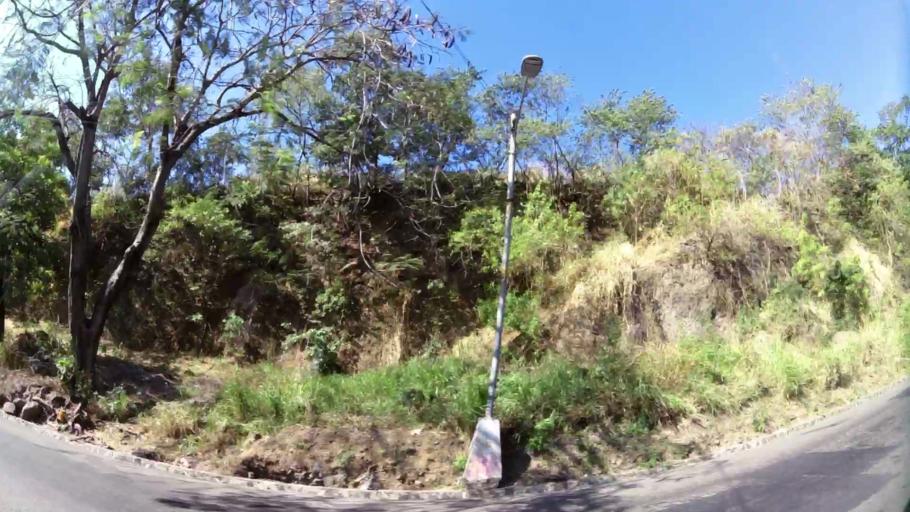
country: SV
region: Sonsonate
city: Sonsonate
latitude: 13.7335
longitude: -89.7323
